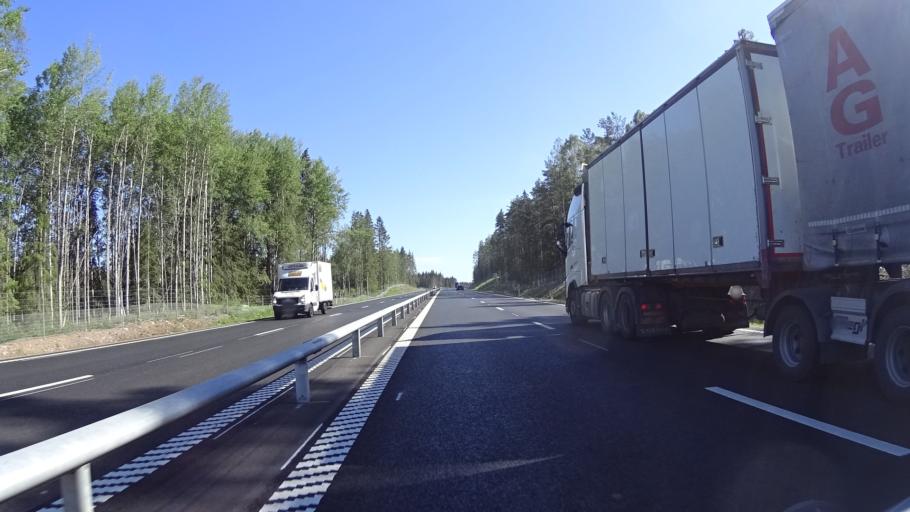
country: SE
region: Vaestra Goetaland
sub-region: Gullspangs Kommun
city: Hova
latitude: 58.8292
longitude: 14.1720
